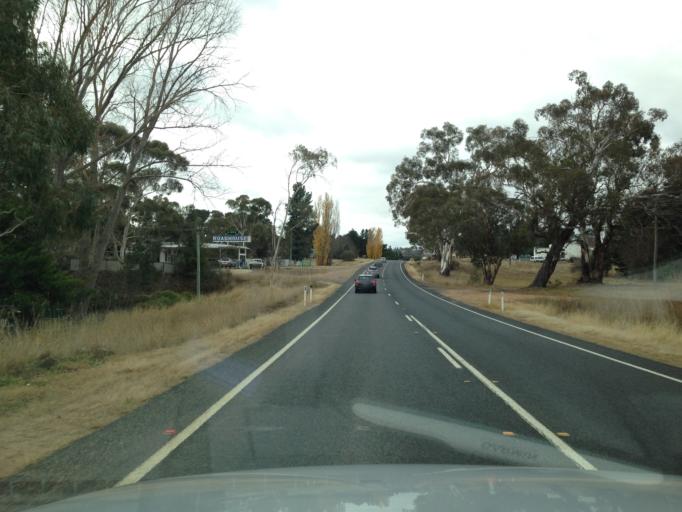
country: AU
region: New South Wales
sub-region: Cooma-Monaro
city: Cooma
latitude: -36.2458
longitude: 149.0540
